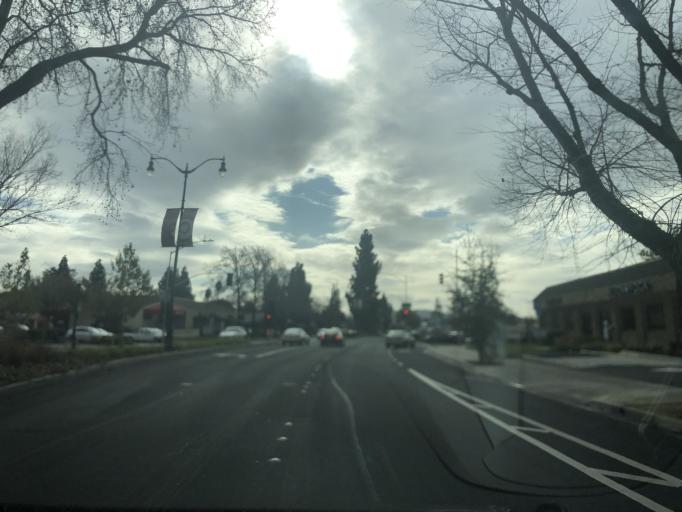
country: US
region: California
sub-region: Contra Costa County
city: Pleasant Hill
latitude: 37.9555
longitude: -122.0602
